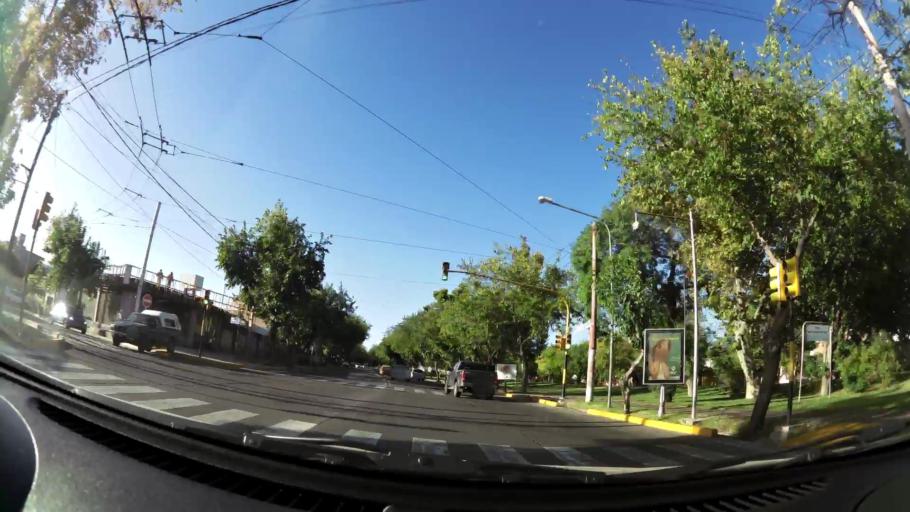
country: AR
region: Mendoza
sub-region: Departamento de Godoy Cruz
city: Godoy Cruz
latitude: -32.9389
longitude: -68.8503
